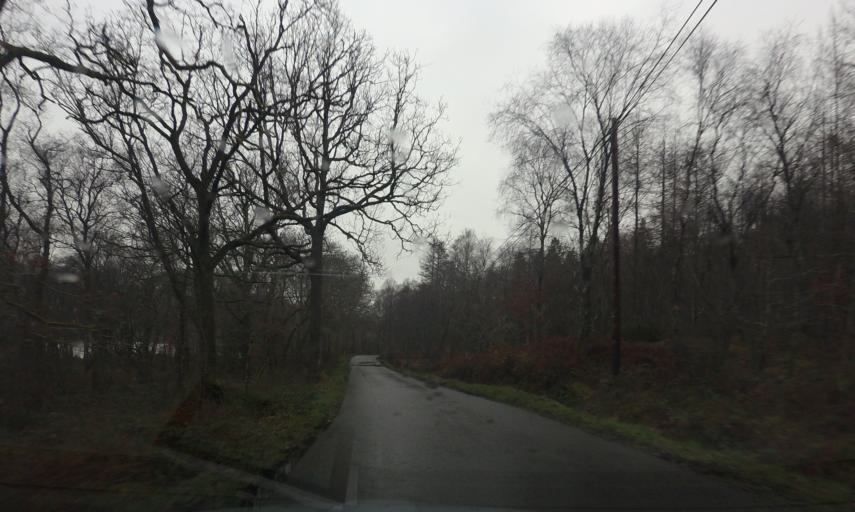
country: GB
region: Scotland
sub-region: West Dunbartonshire
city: Balloch
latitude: 56.1261
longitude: -4.6040
